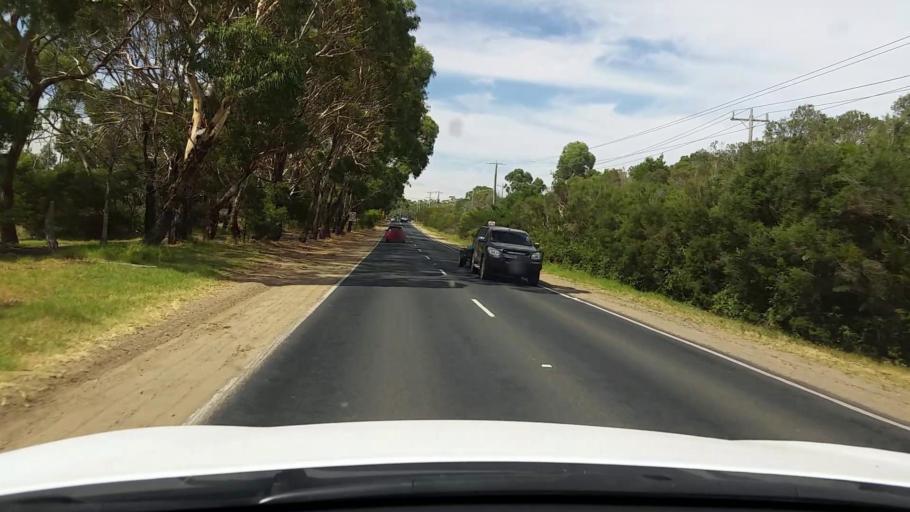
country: AU
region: Victoria
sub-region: Mornington Peninsula
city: Hastings
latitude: -38.3256
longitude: 145.1829
